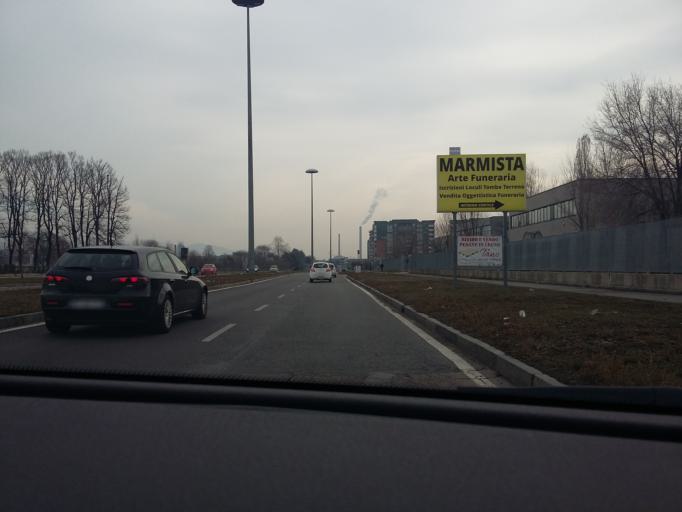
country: IT
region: Piedmont
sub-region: Provincia di Torino
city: Fornaci
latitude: 45.0351
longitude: 7.6076
